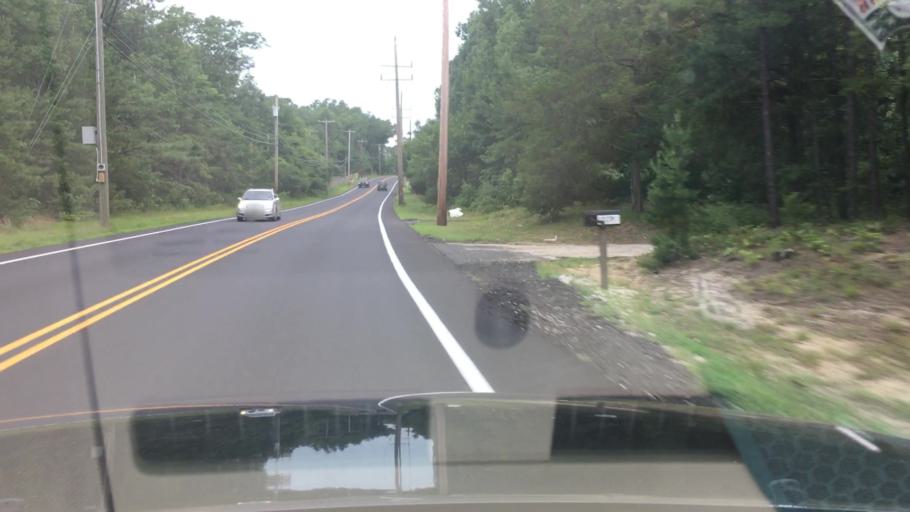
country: US
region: New Jersey
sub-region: Ocean County
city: Cedar Glen West
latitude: 40.0472
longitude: -74.3273
